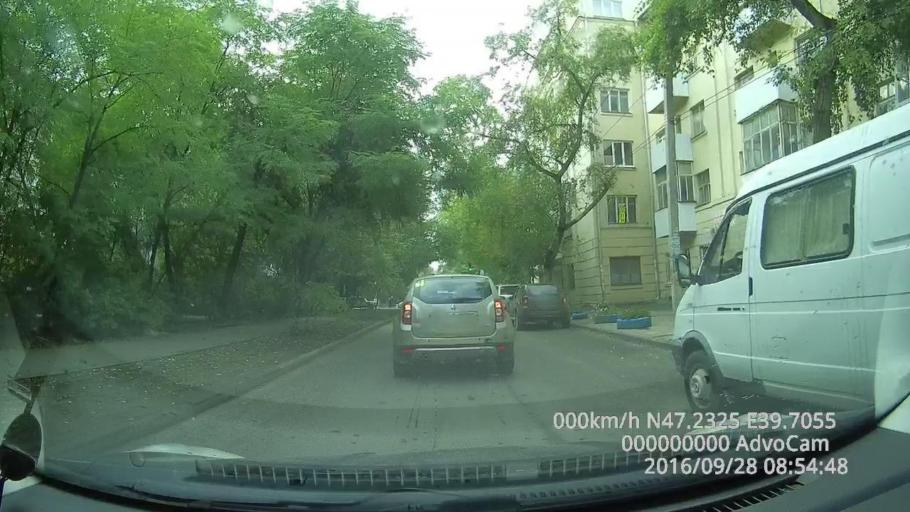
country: RU
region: Rostov
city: Rostov-na-Donu
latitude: 47.2325
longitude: 39.7056
